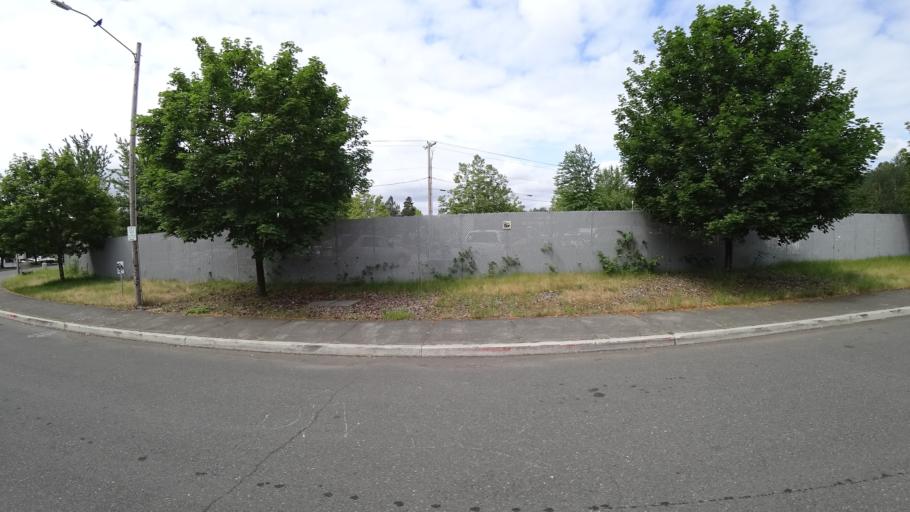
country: US
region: Washington
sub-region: Clark County
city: Vancouver
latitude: 45.6195
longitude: -122.6932
